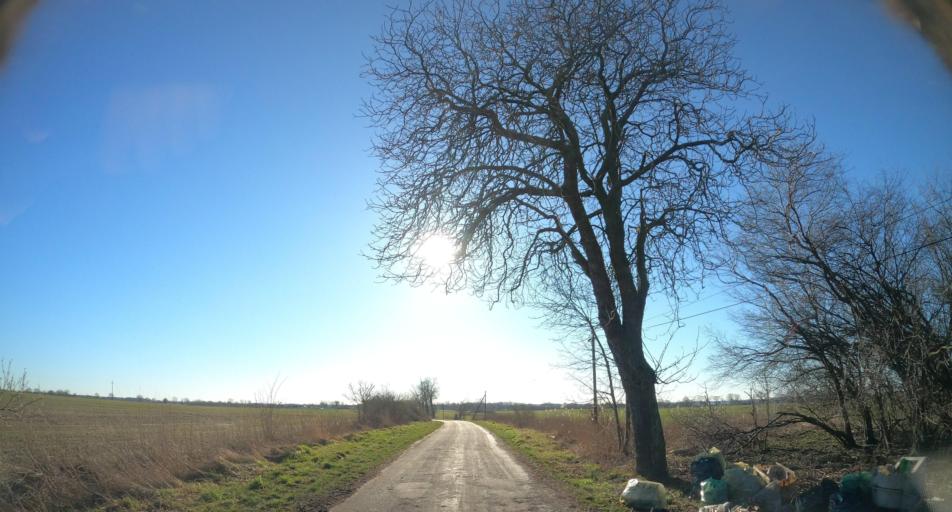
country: PL
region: West Pomeranian Voivodeship
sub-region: Powiat kamienski
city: Dziwnow
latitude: 54.0224
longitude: 14.8265
